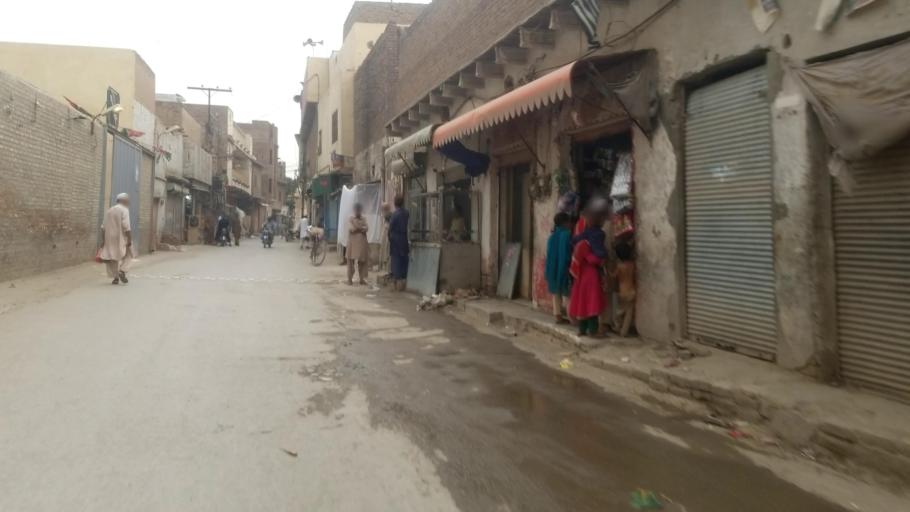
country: PK
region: Khyber Pakhtunkhwa
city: Peshawar
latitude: 33.9894
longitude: 71.5527
